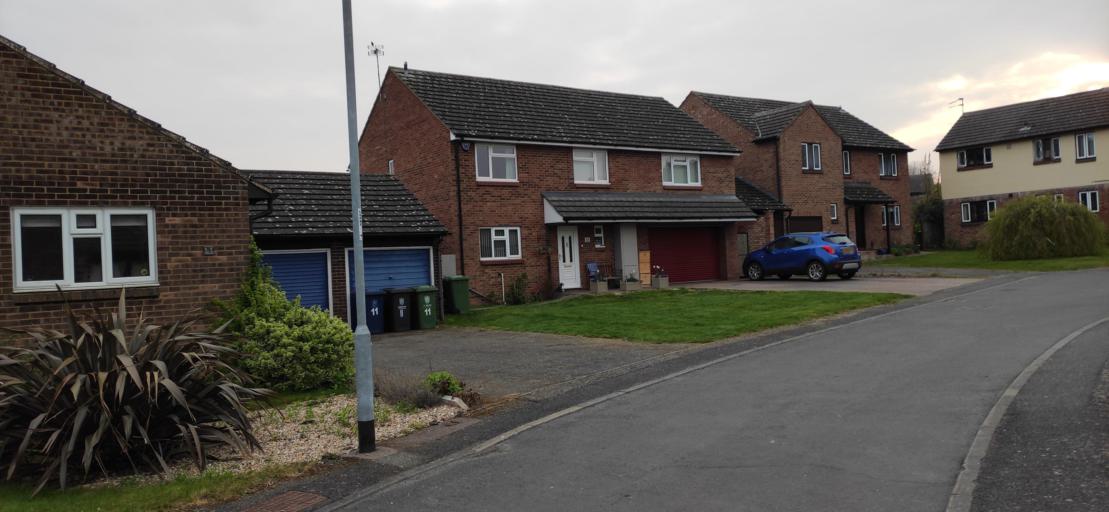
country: GB
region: England
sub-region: Cambridgeshire
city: Swavesey
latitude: 52.2490
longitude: 0.0176
